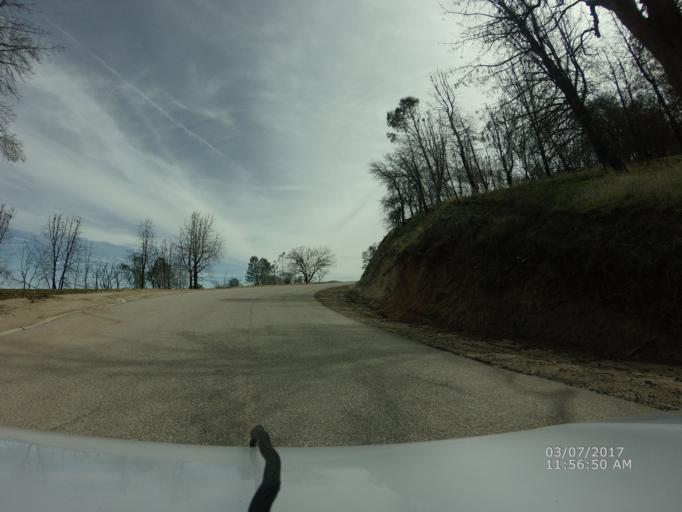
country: US
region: California
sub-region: Kern County
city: Lebec
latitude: 34.7573
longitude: -118.7179
